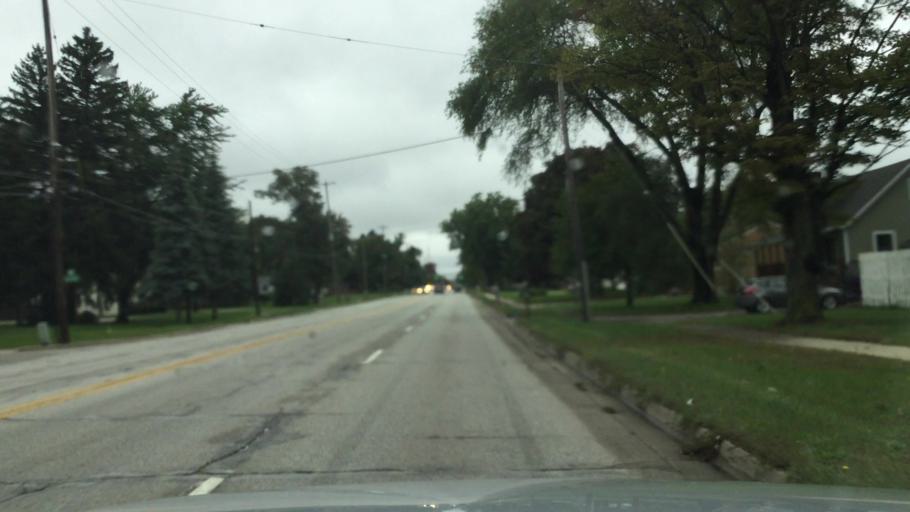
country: US
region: Michigan
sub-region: Saginaw County
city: Shields
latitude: 43.4402
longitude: -84.0147
